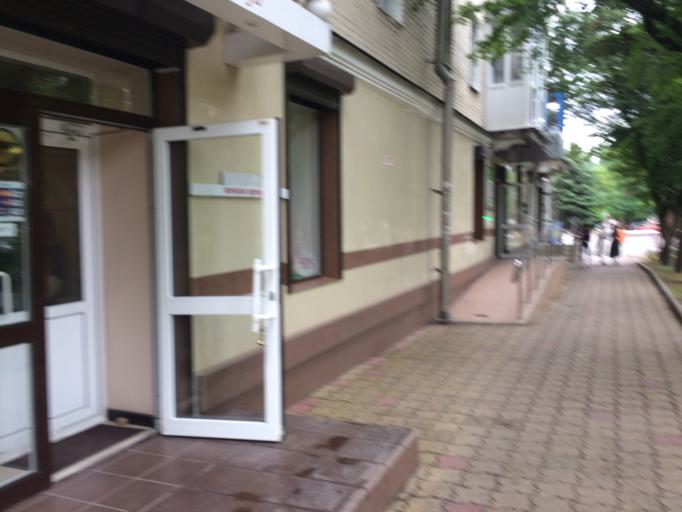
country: RU
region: Stavropol'skiy
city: Stavropol'
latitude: 45.0391
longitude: 41.9636
